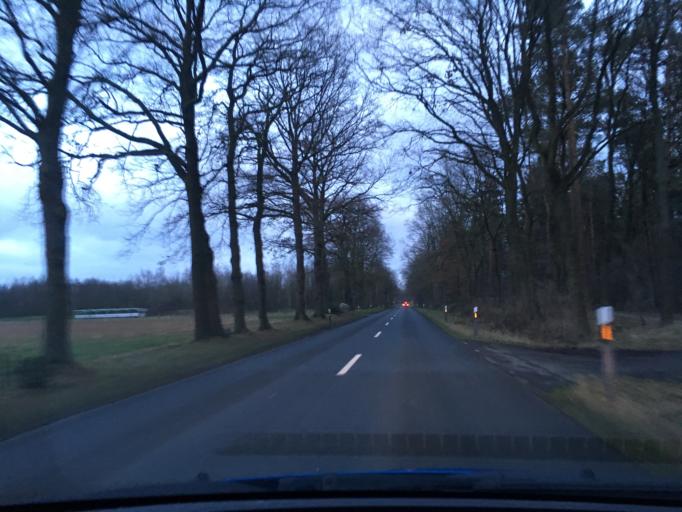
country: DE
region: Lower Saxony
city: Radbruch
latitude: 53.3136
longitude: 10.2702
